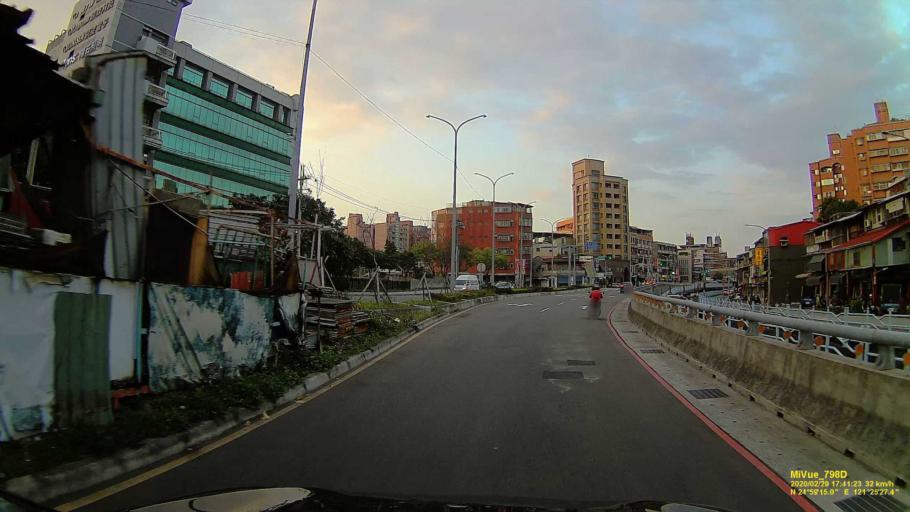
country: TW
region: Taipei
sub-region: Taipei
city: Banqiao
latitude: 24.9877
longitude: 121.4243
